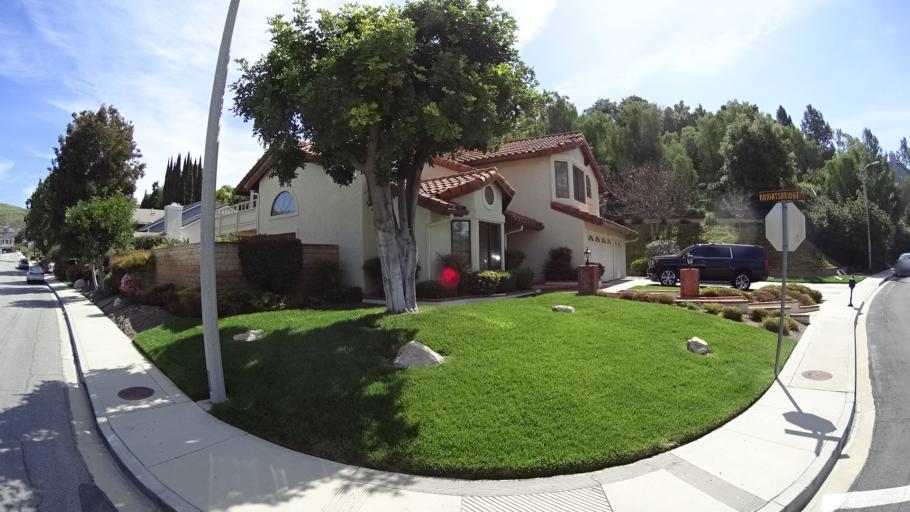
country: US
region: California
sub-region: Ventura County
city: Thousand Oaks
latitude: 34.2184
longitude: -118.8327
